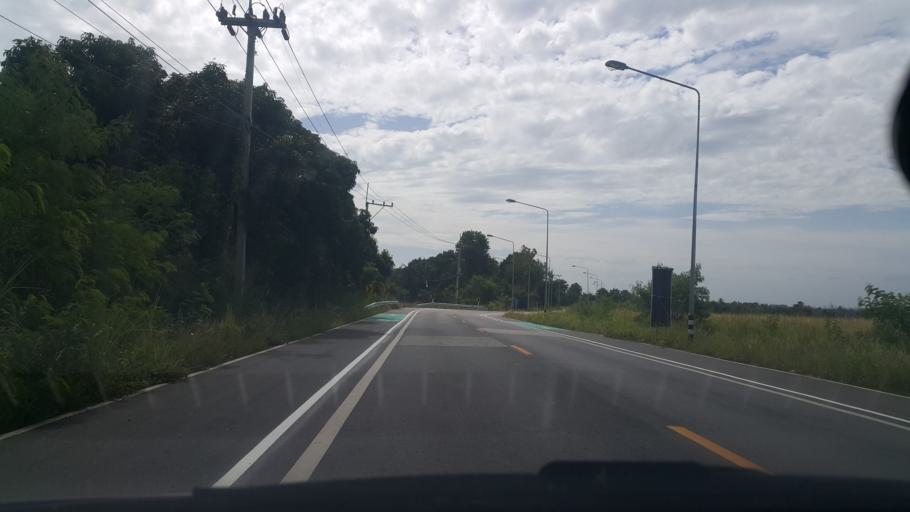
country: TH
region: Rayong
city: Ban Chang
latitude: 12.7780
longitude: 100.9586
